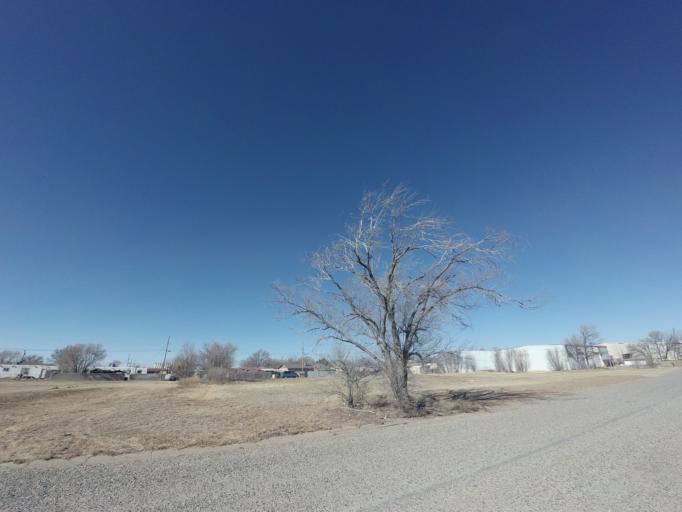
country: US
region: New Mexico
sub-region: Curry County
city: Clovis
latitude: 34.4026
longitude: -103.2398
